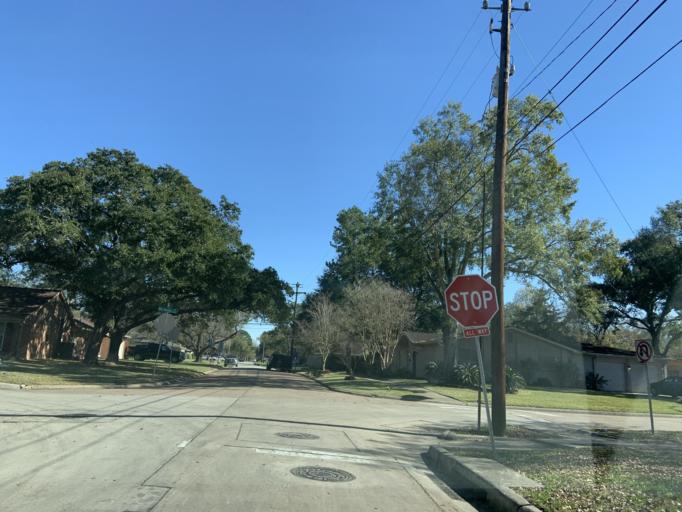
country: US
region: Texas
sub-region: Harris County
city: Bellaire
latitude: 29.6851
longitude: -95.5039
